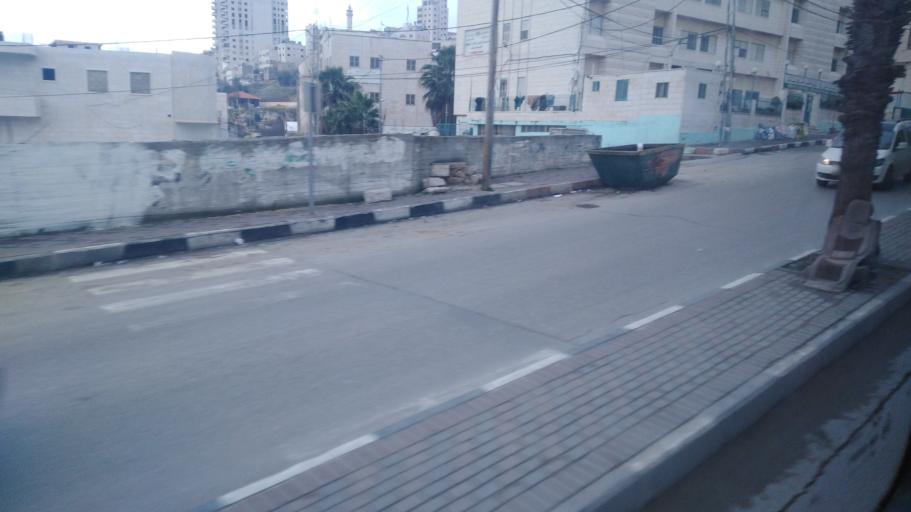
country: PS
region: West Bank
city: Hebron
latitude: 31.5303
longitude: 35.0891
